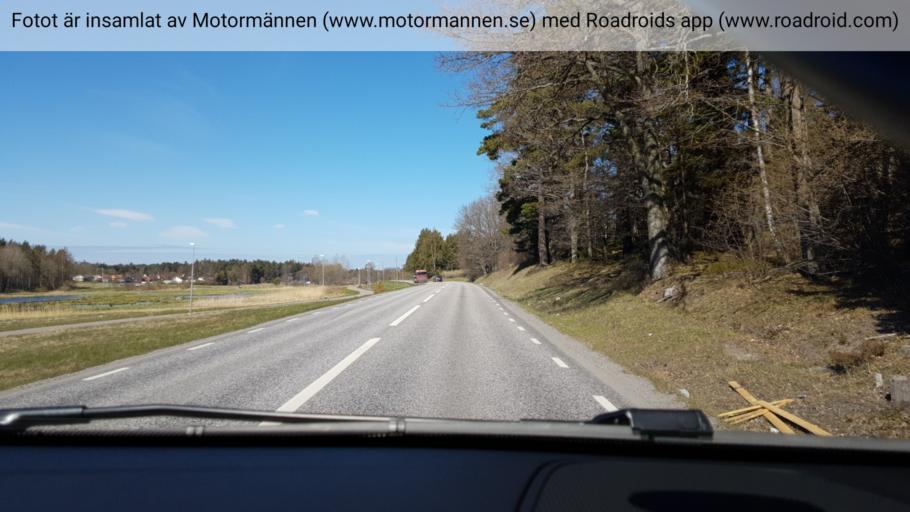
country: SE
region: Stockholm
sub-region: Varmdo Kommun
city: Hemmesta
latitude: 59.3257
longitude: 18.5171
